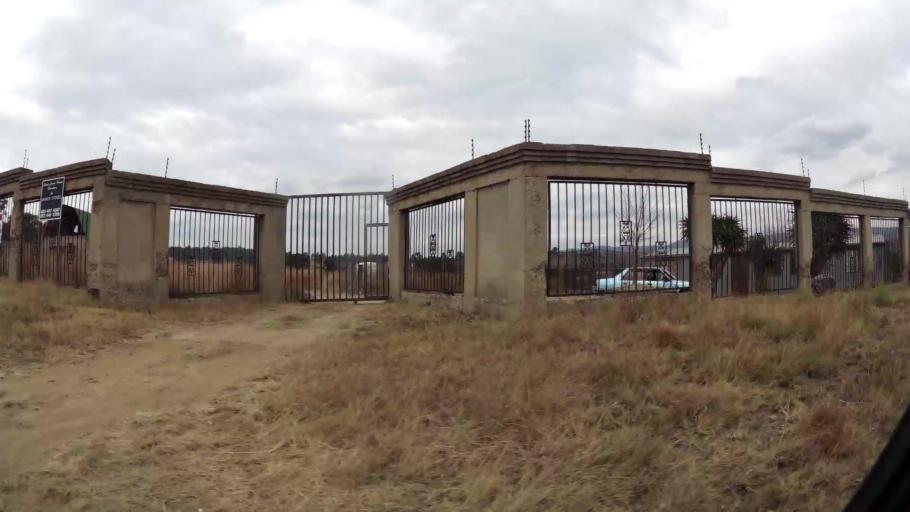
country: ZA
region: Gauteng
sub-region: West Rand District Municipality
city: Muldersdriseloop
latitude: -26.0568
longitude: 27.8831
